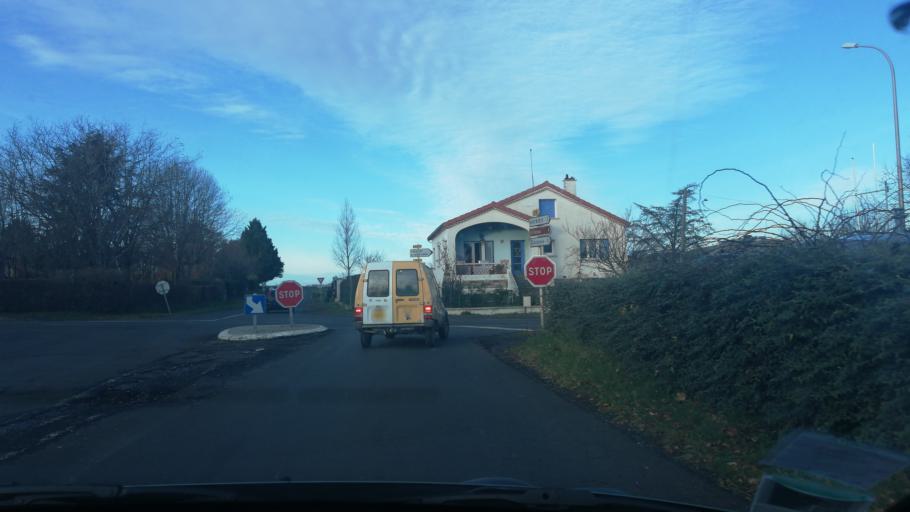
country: FR
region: Auvergne
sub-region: Departement du Puy-de-Dome
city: Billom
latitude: 45.7231
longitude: 3.3513
